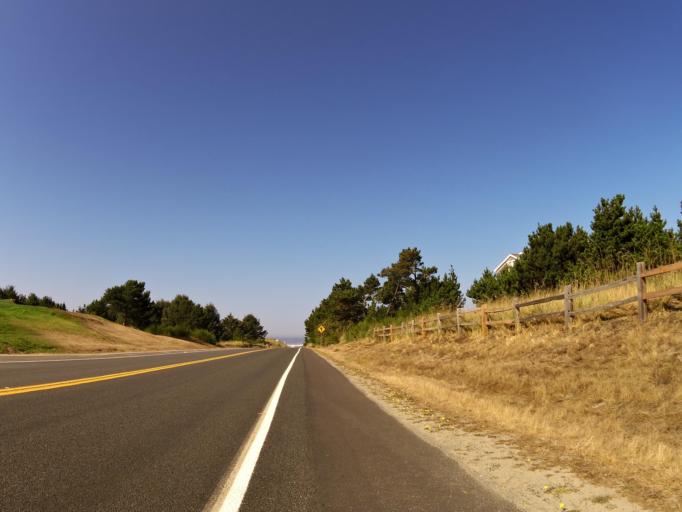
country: US
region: Oregon
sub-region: Clatsop County
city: Gearhart
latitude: 46.0486
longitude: -123.9249
